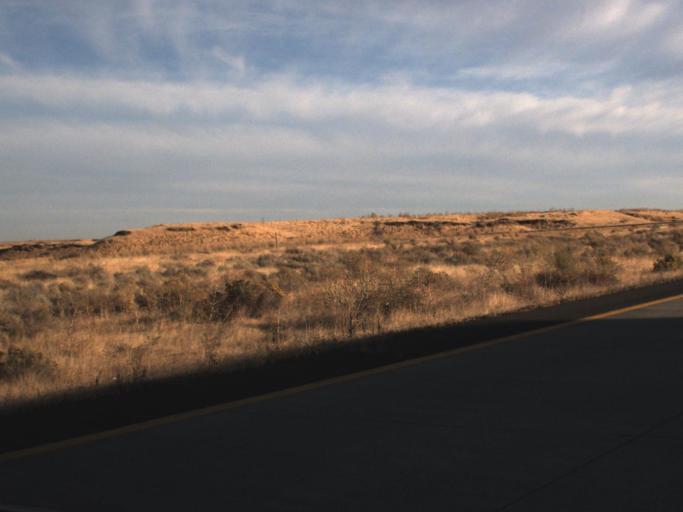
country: US
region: Washington
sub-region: Franklin County
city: Connell
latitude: 46.5868
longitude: -118.9645
